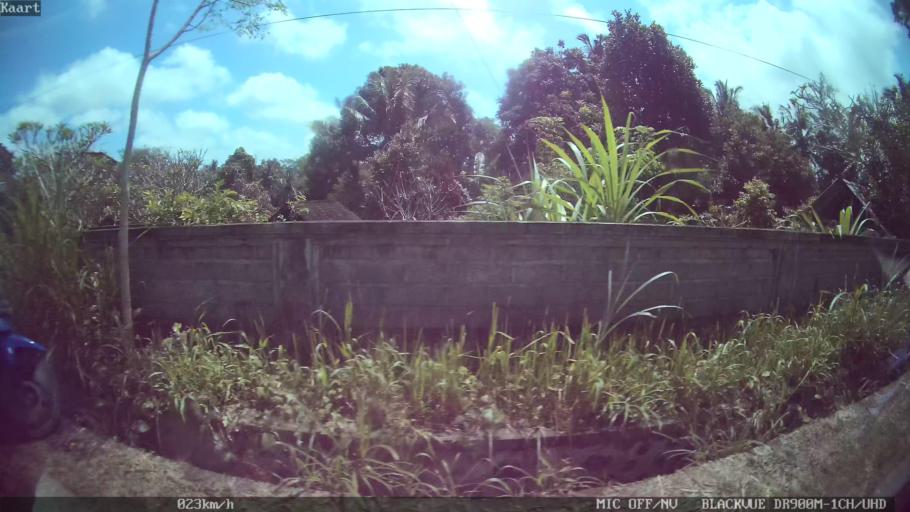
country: ID
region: Bali
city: Banjar Apuan Kaja
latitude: -8.5016
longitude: 115.3394
